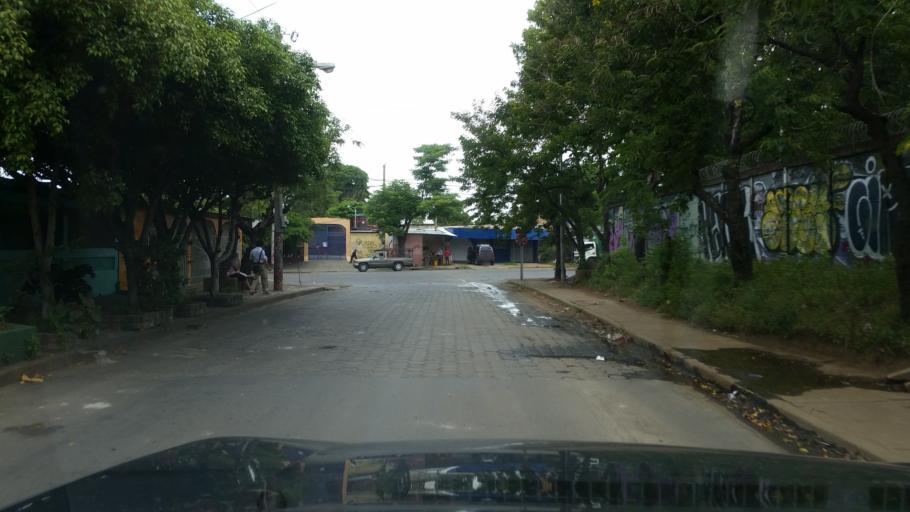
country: NI
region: Managua
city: Managua
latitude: 12.1359
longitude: -86.2175
